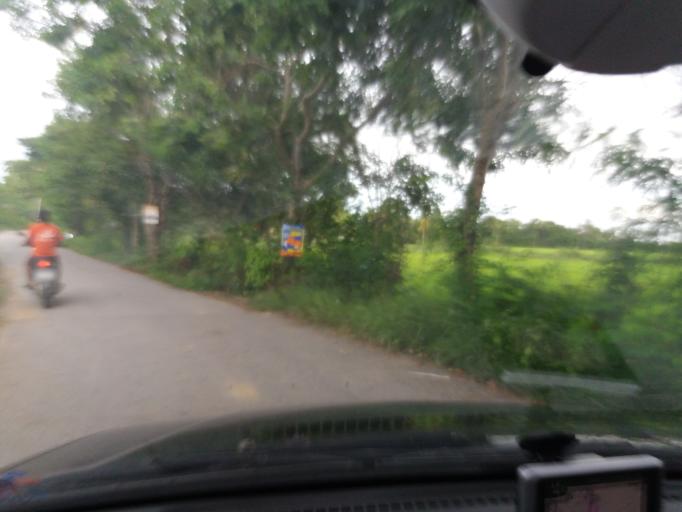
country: TH
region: Suphan Buri
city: Doembang Nangbuat
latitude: 14.8175
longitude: 100.1366
